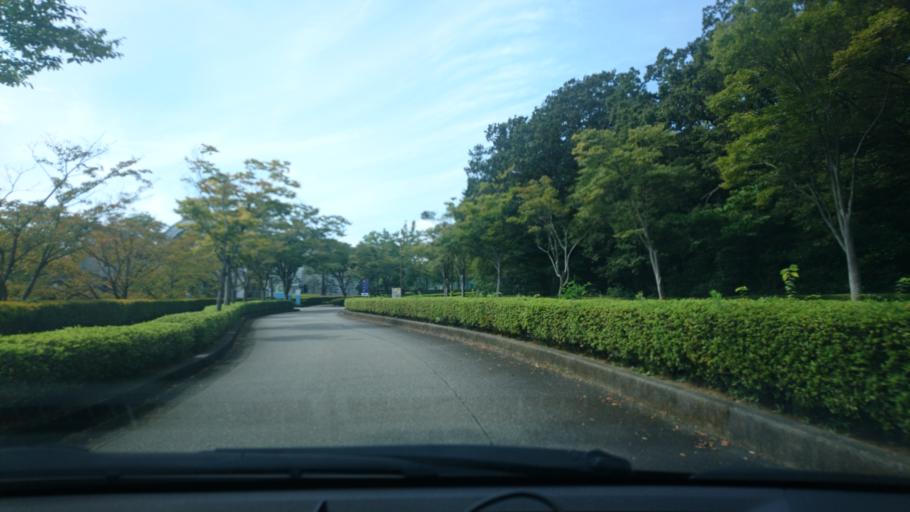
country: JP
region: Ishikawa
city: Komatsu
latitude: 36.3252
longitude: 136.3327
